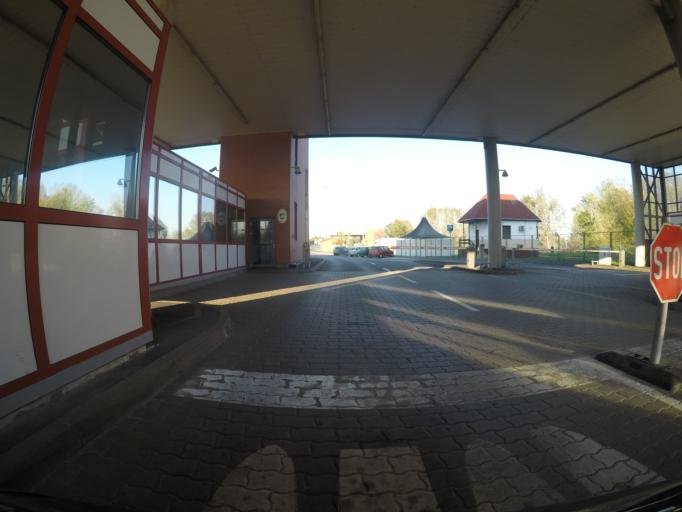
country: HU
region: Somogy
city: Barcs
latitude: 45.9477
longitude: 17.4626
